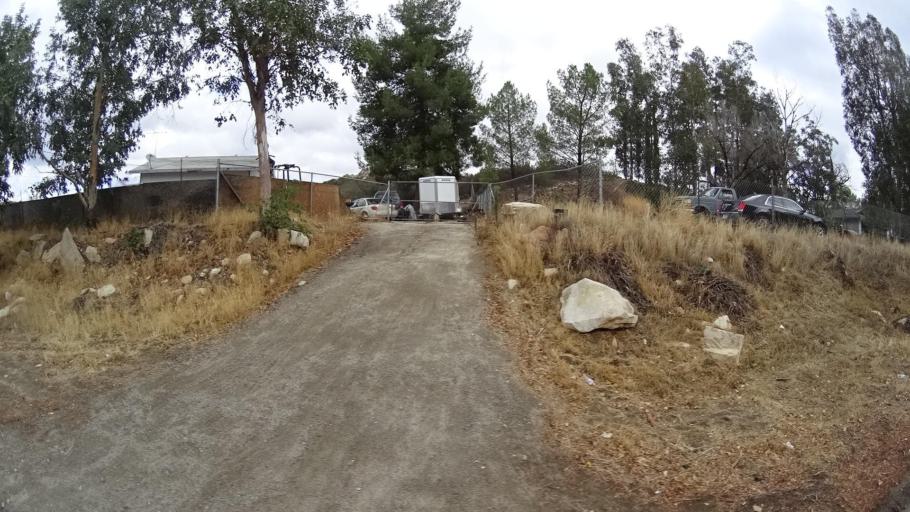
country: US
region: California
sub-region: San Diego County
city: Campo
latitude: 32.6305
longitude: -116.4288
